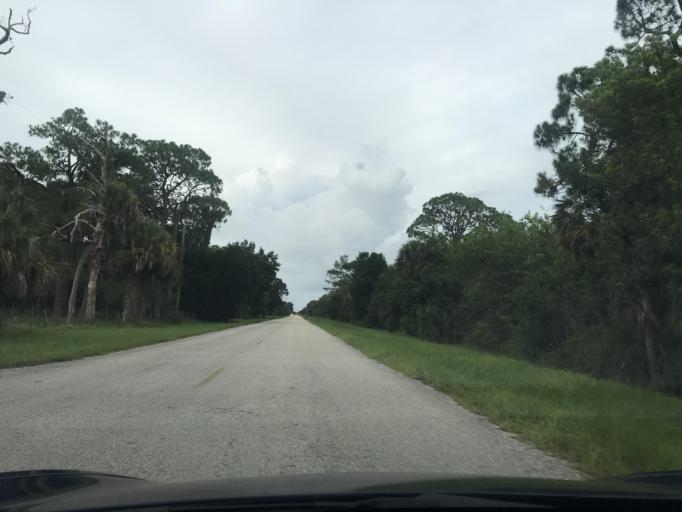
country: US
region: Florida
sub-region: Indian River County
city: West Vero Corridor
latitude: 27.6172
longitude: -80.4942
